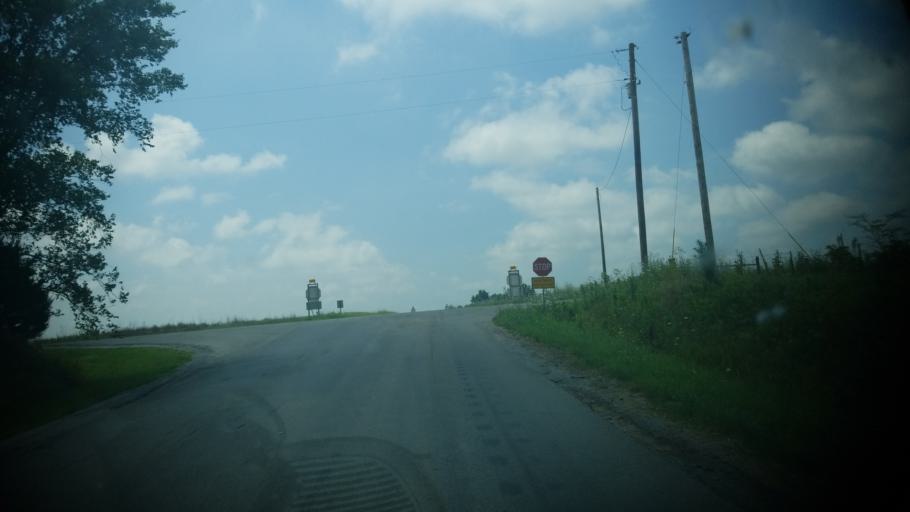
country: US
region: Illinois
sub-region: Wayne County
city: Fairfield
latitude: 38.5121
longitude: -88.3484
